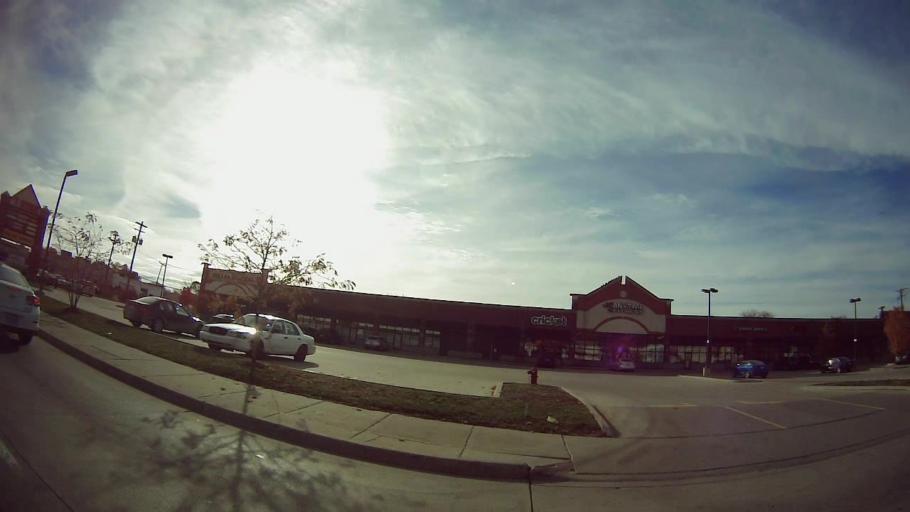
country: US
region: Michigan
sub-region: Macomb County
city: Warren
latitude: 42.4631
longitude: -83.0283
